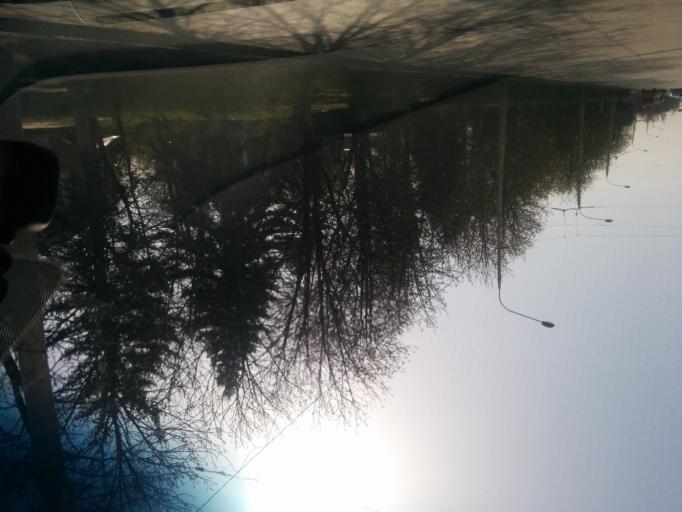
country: RU
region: Rostov
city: Shakhty
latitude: 47.7006
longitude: 40.2097
